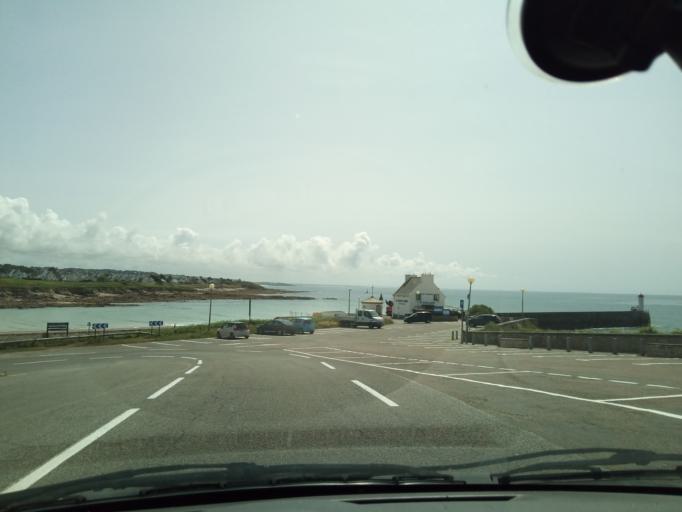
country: FR
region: Brittany
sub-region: Departement du Finistere
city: Audierne
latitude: 48.0118
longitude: -4.5425
